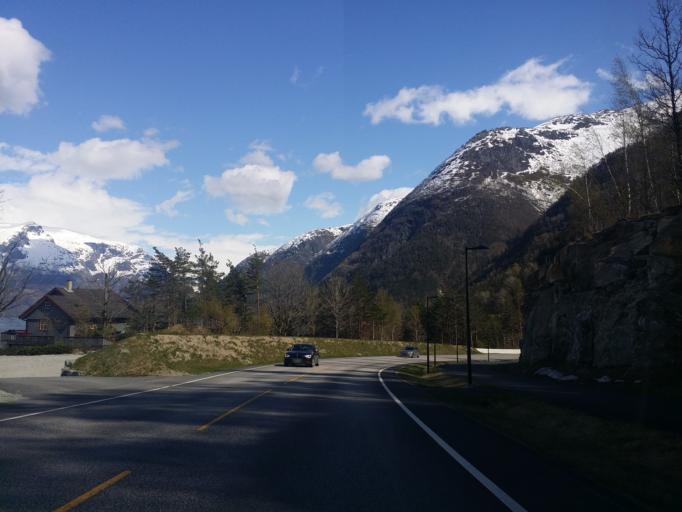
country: NO
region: Hordaland
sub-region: Ulvik
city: Ulvik
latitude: 60.4695
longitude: 6.8672
